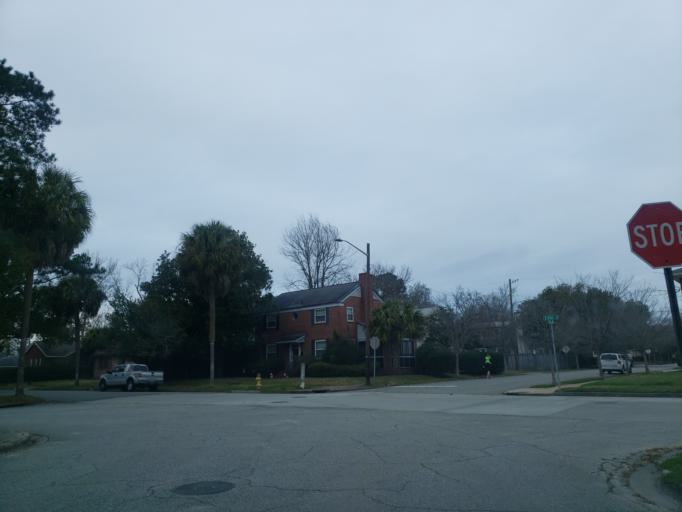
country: US
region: Georgia
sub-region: Chatham County
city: Savannah
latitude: 32.0413
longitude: -81.0944
